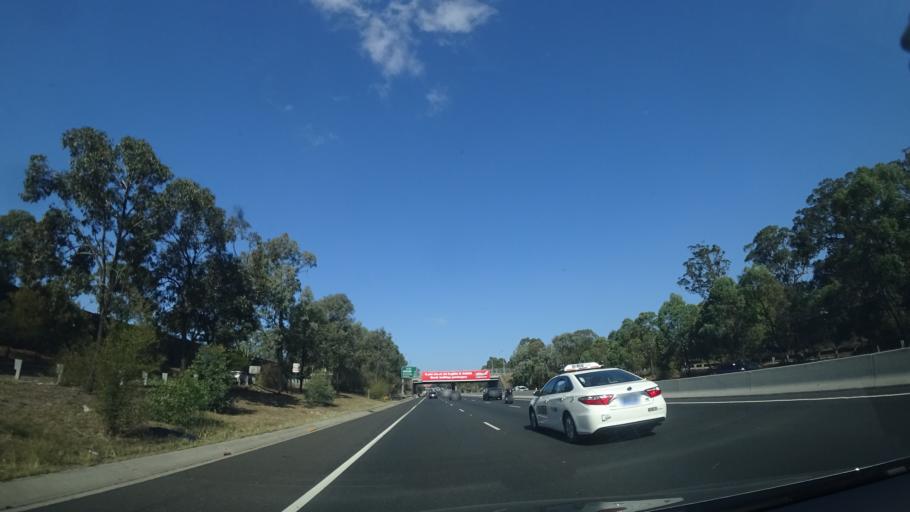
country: AU
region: New South Wales
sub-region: Hurstville
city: Peakhurst
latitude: -33.9424
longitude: 151.0519
